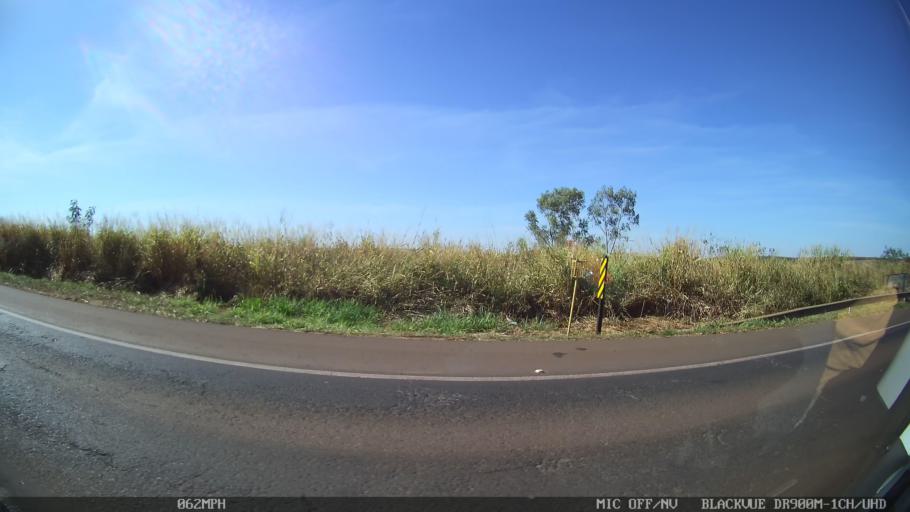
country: BR
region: Sao Paulo
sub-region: Olimpia
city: Olimpia
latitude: -20.7152
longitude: -48.8753
